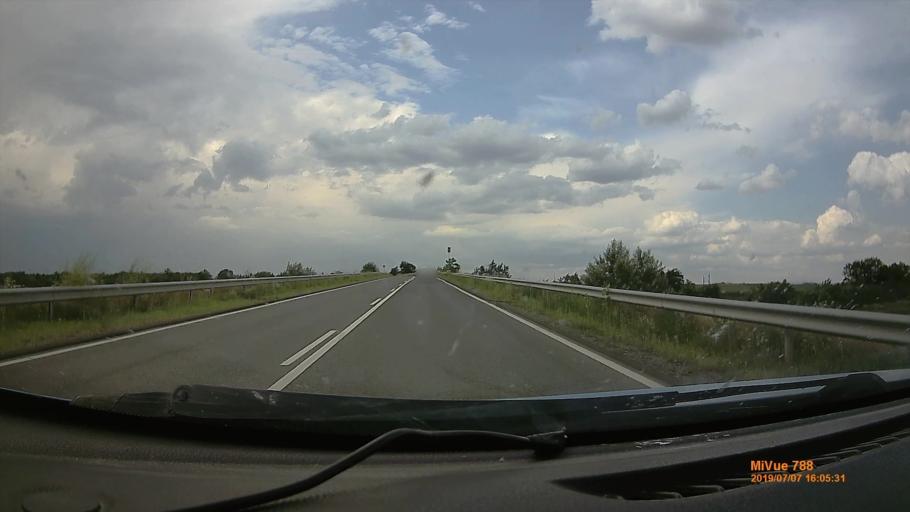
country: HU
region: Heves
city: Hatvan
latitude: 47.6637
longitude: 19.7228
